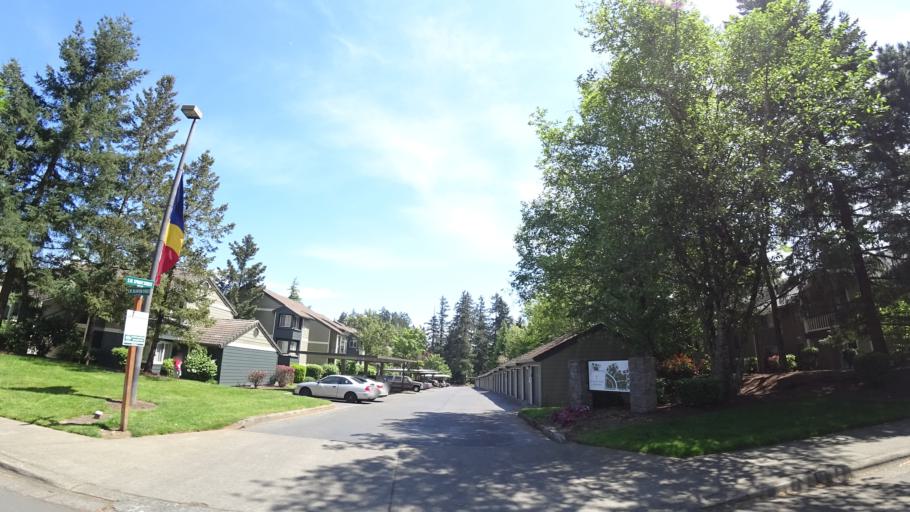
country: US
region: Oregon
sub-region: Washington County
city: Aloha
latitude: 45.4879
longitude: -122.8370
